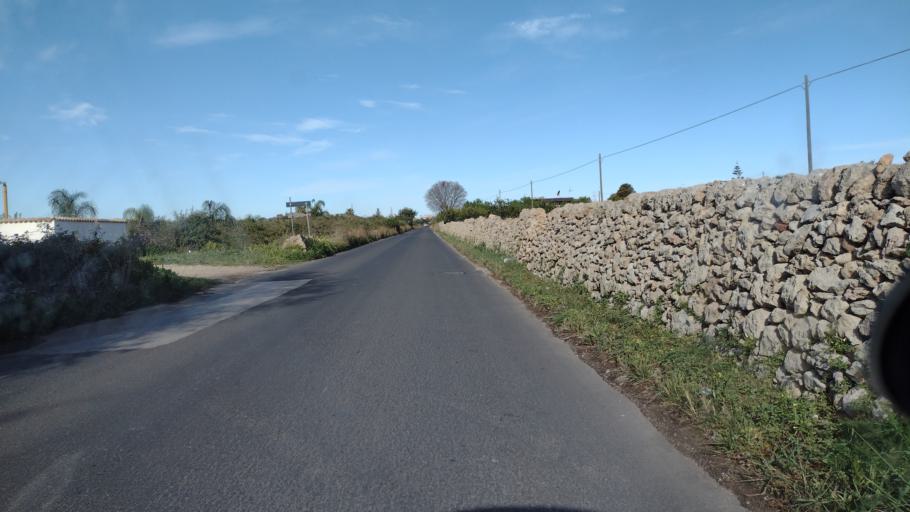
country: IT
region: Sicily
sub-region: Provincia di Siracusa
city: Avola
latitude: 36.8722
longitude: 15.1232
